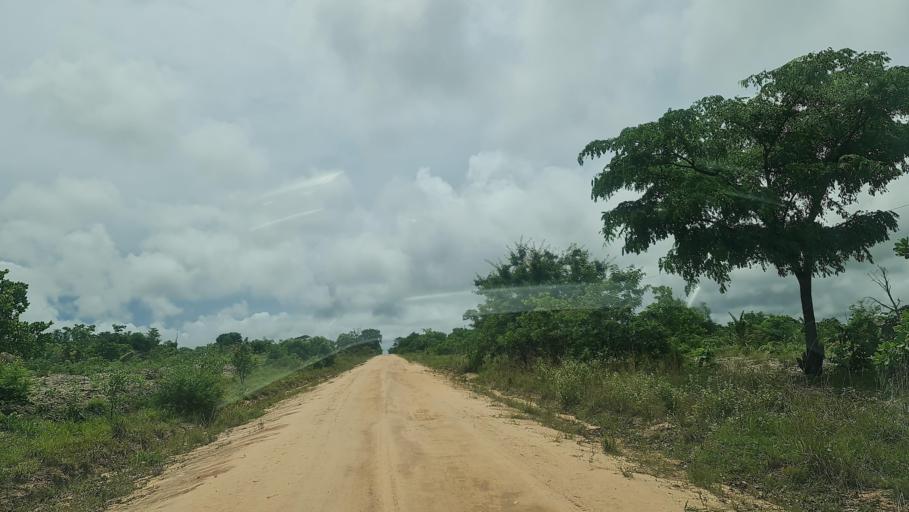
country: MZ
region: Zambezia
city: Quelimane
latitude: -17.2527
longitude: 37.2210
